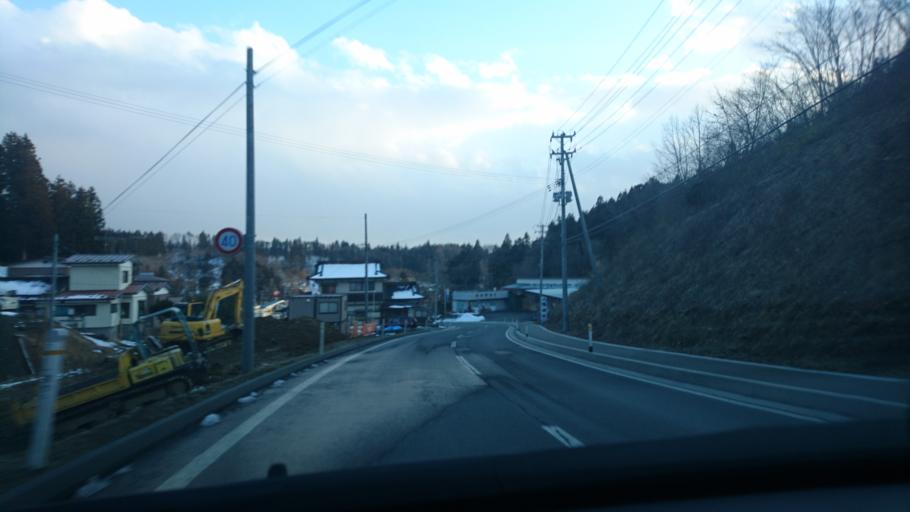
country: JP
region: Iwate
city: Ichinoseki
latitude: 39.0005
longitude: 141.3334
